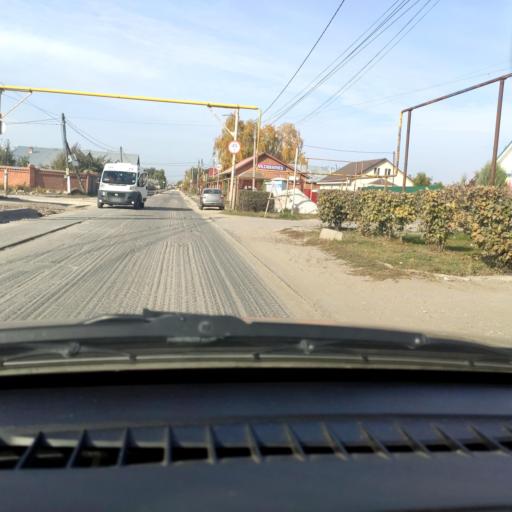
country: RU
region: Samara
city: Podstepki
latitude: 53.5105
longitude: 49.2397
